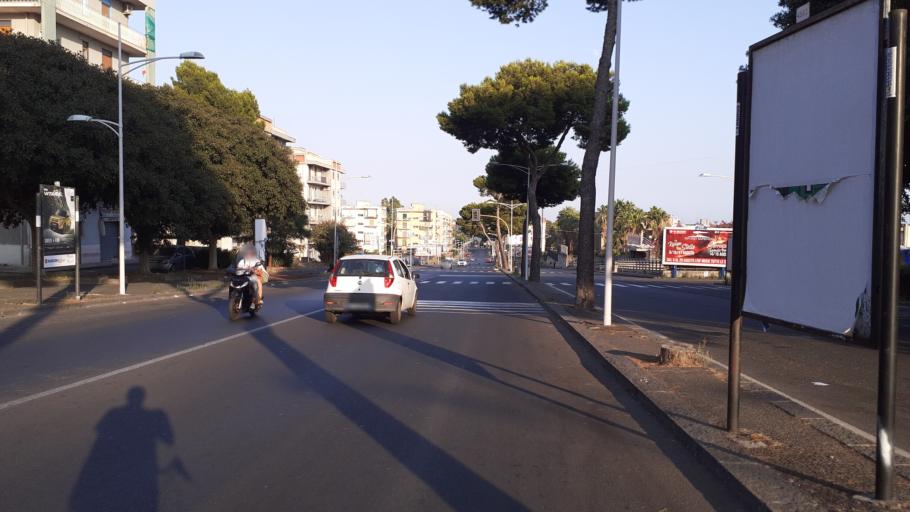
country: IT
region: Sicily
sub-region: Catania
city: Catania
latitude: 37.5054
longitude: 15.0539
